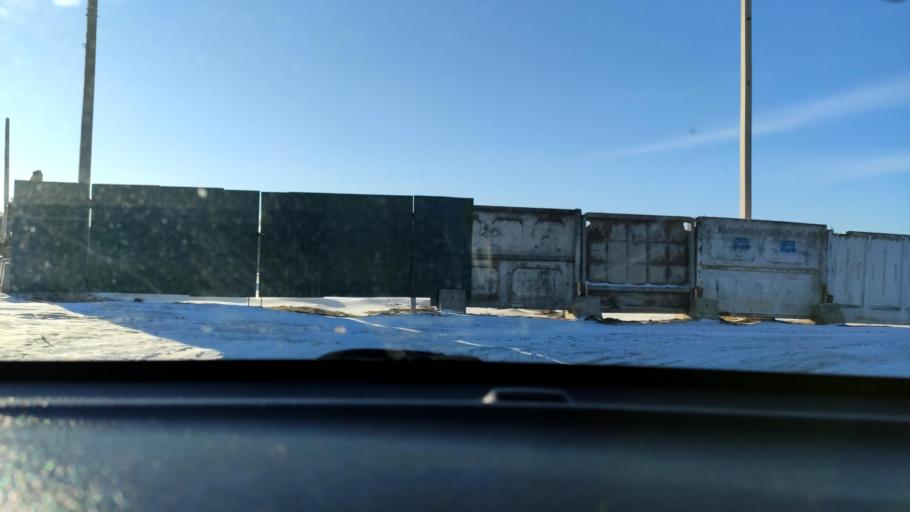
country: RU
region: Voronezj
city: Podgornoye
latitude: 51.7219
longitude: 39.1352
